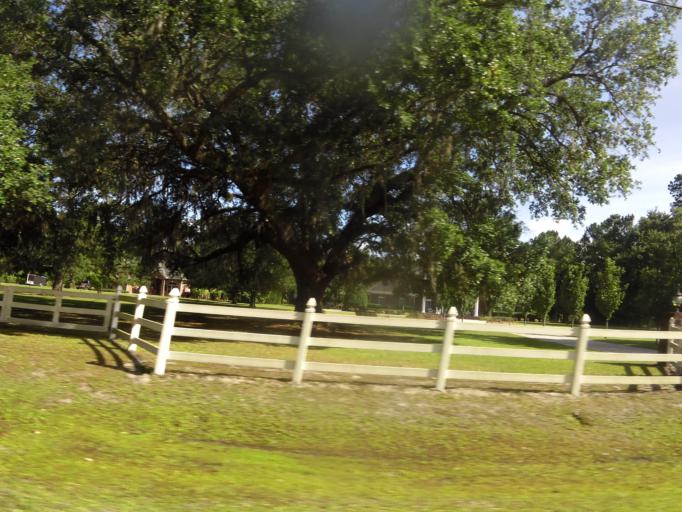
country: US
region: Florida
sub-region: Nassau County
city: Callahan
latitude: 30.5591
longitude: -81.8610
